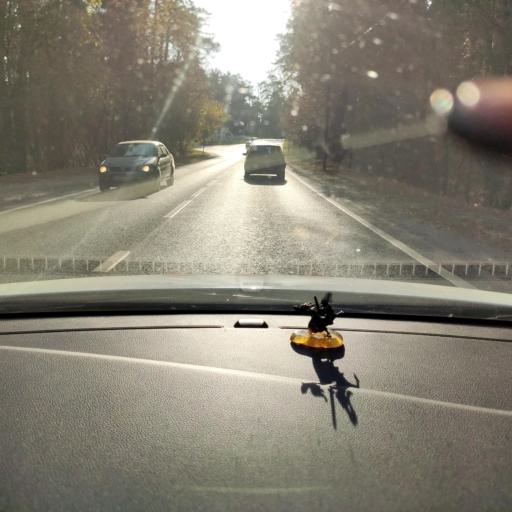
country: RU
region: Tatarstan
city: Osinovo
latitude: 55.8275
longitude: 48.8953
